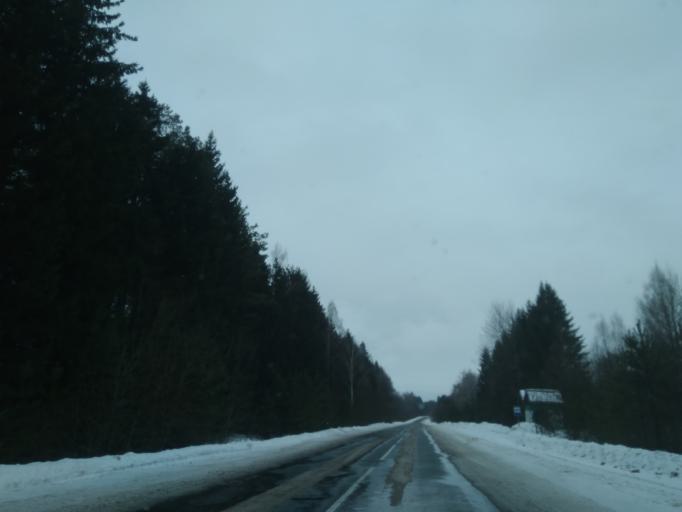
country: BY
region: Minsk
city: Ivyanyets
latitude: 53.8469
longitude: 26.7915
